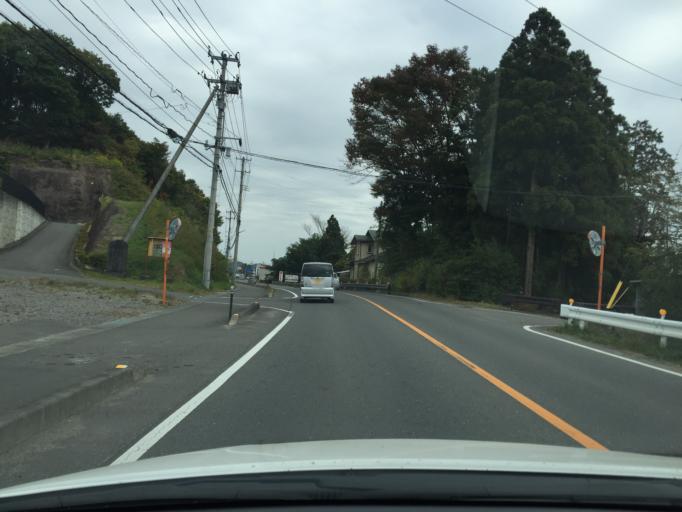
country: JP
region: Tochigi
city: Kuroiso
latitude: 37.1304
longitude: 140.1834
